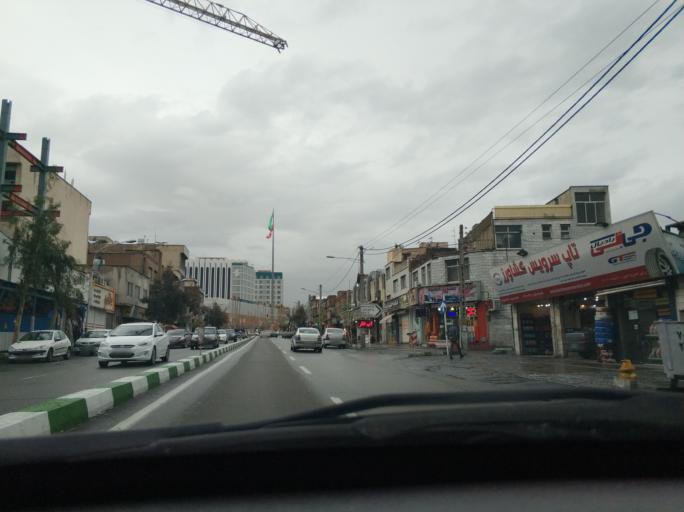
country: IR
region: Tehran
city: Tehran
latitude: 35.7049
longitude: 51.4397
